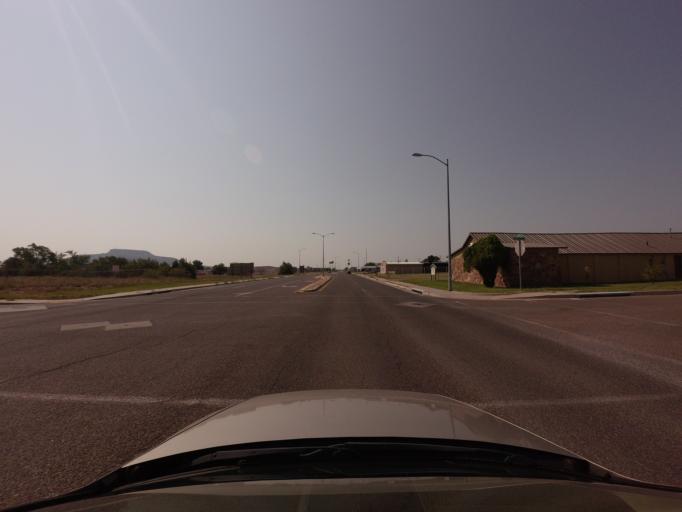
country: US
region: New Mexico
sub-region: Quay County
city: Tucumcari
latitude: 35.1609
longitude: -103.7250
